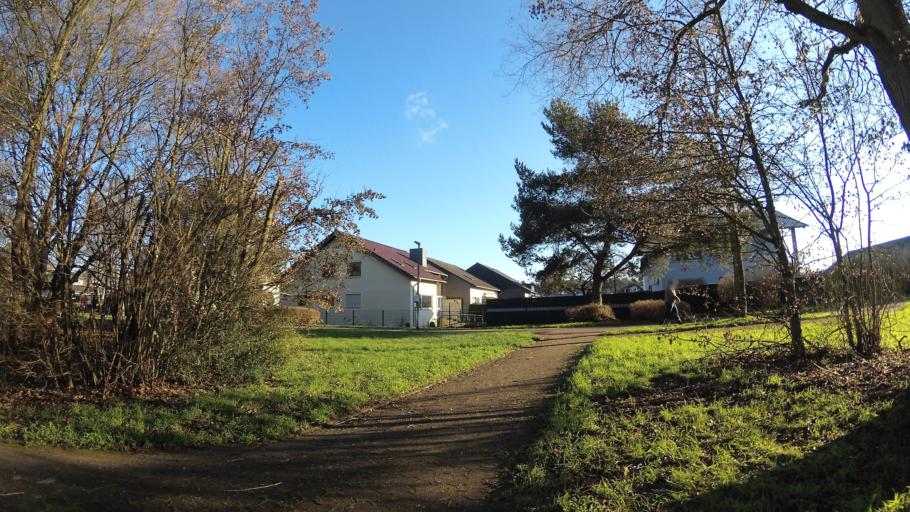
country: DE
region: Saarland
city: Saarwellingen
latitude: 49.3378
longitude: 6.7795
